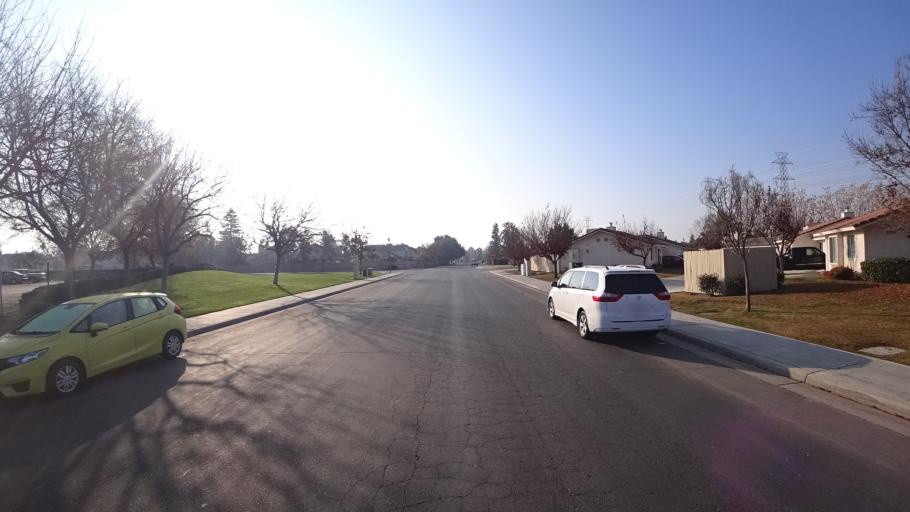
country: US
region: California
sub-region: Kern County
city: Greenacres
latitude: 35.3304
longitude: -119.0952
